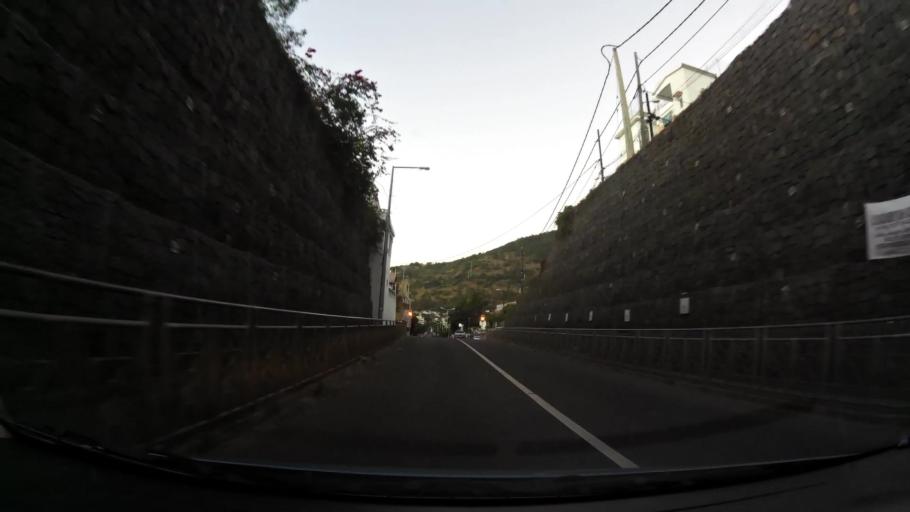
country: MU
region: Port Louis
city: Port Louis
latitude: -20.1684
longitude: 57.5145
